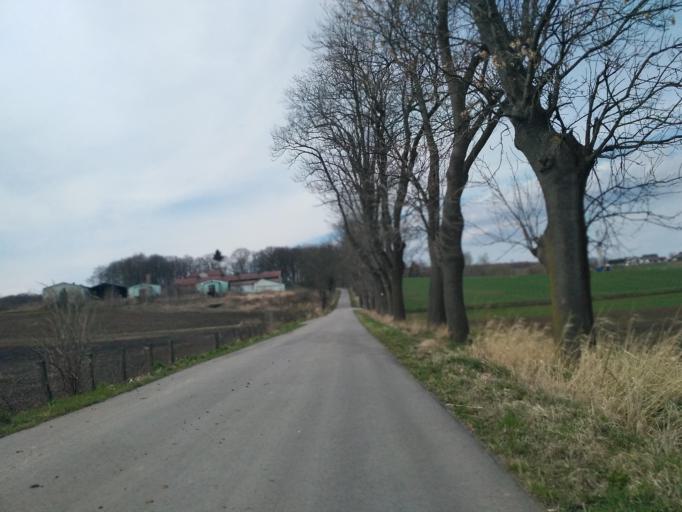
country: PL
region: Subcarpathian Voivodeship
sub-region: Powiat ropczycko-sedziszowski
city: Iwierzyce
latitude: 50.0408
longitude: 21.7435
